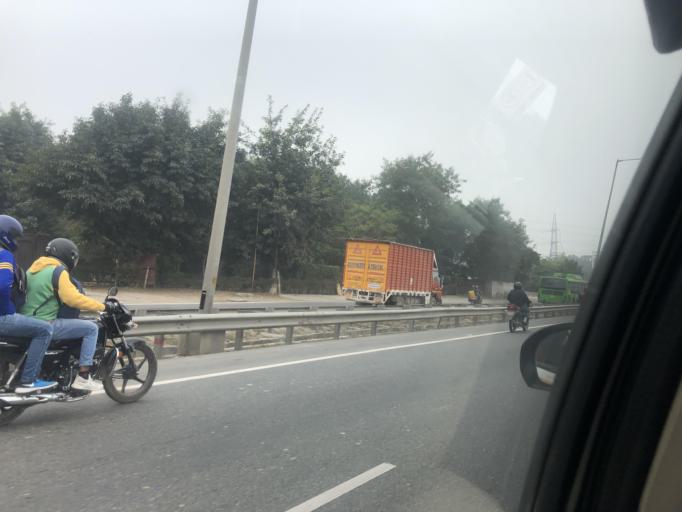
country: IN
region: Haryana
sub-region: Gurgaon
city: Gurgaon
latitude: 28.5274
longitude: 77.1023
